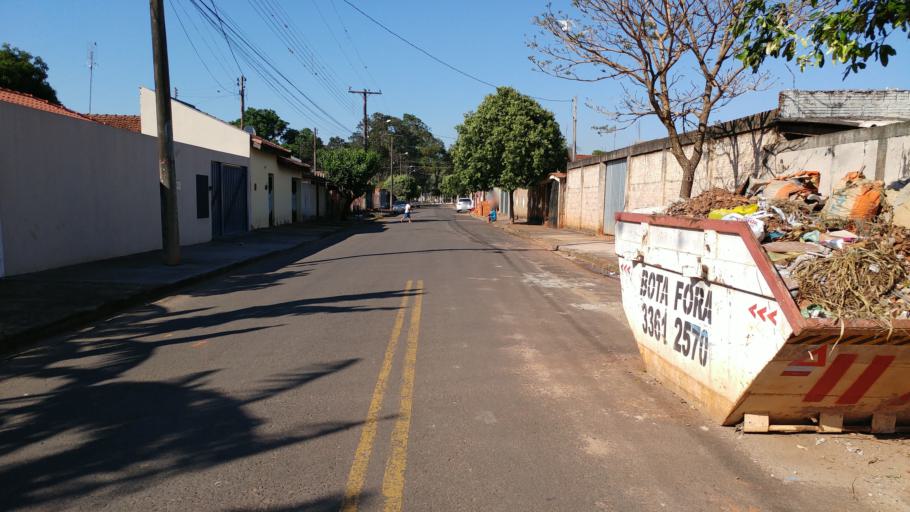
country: BR
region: Sao Paulo
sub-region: Paraguacu Paulista
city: Paraguacu Paulista
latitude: -22.4194
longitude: -50.5706
